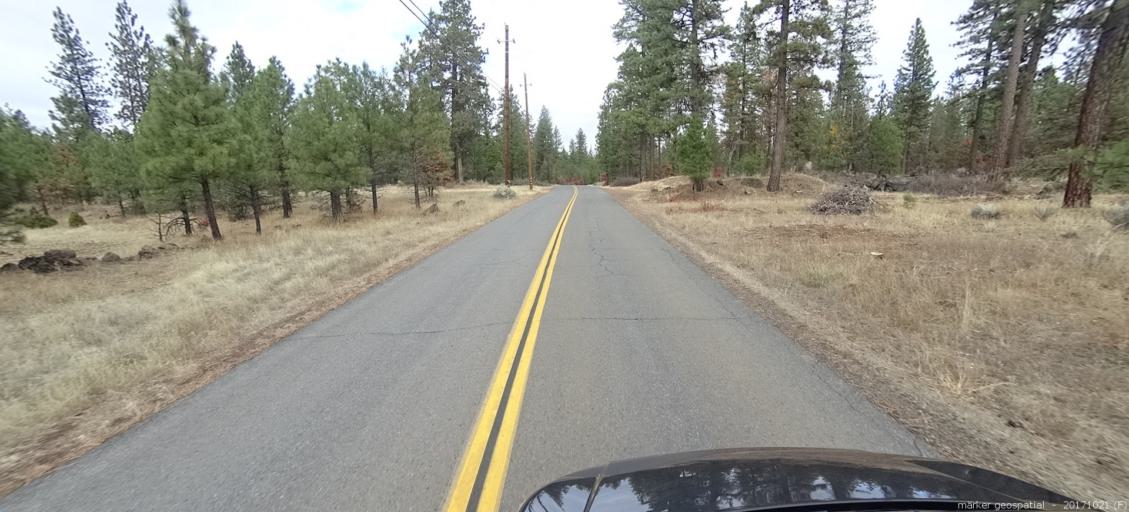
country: US
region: California
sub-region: Shasta County
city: Burney
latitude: 40.9280
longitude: -121.6452
